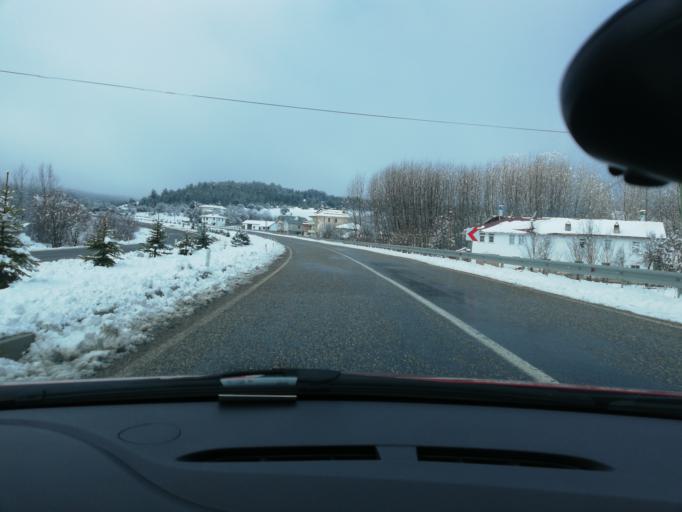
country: TR
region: Kastamonu
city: Ihsangazi
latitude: 41.3034
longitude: 33.5438
